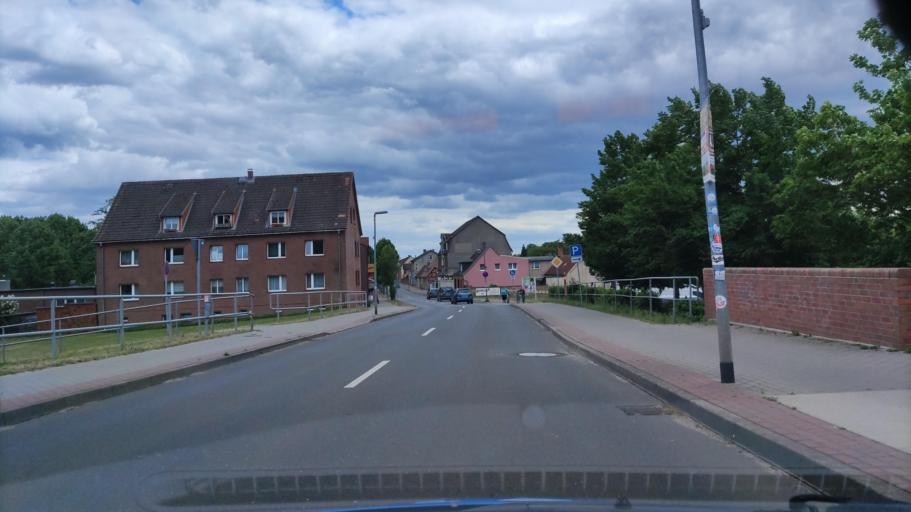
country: DE
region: Mecklenburg-Vorpommern
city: Neustadt-Glewe
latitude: 53.3812
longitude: 11.5885
